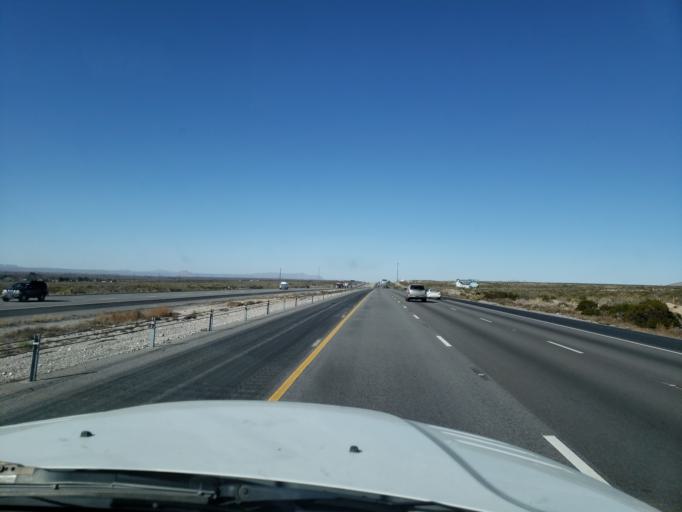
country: US
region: New Mexico
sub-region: Dona Ana County
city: Mesquite
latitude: 32.2089
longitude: -106.6948
